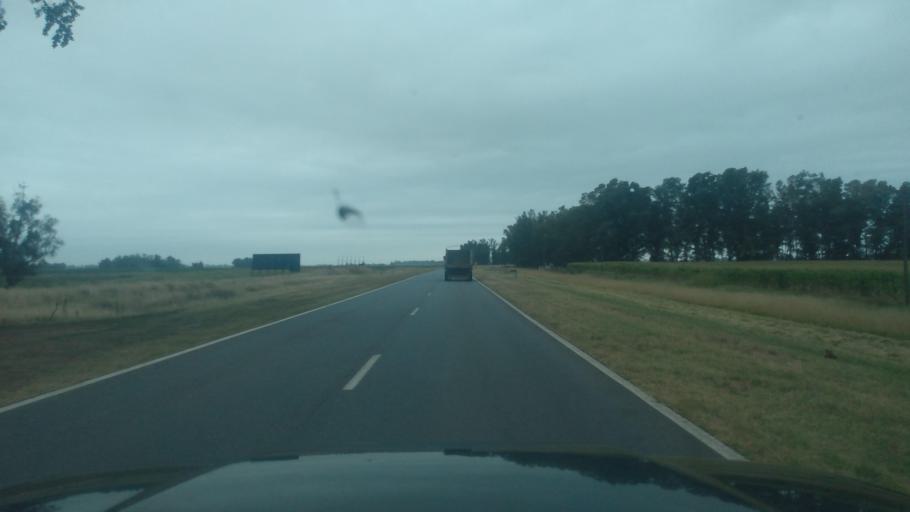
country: AR
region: Buenos Aires
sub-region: Partido de Nueve de Julio
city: Nueve de Julio
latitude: -35.4046
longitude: -60.7695
